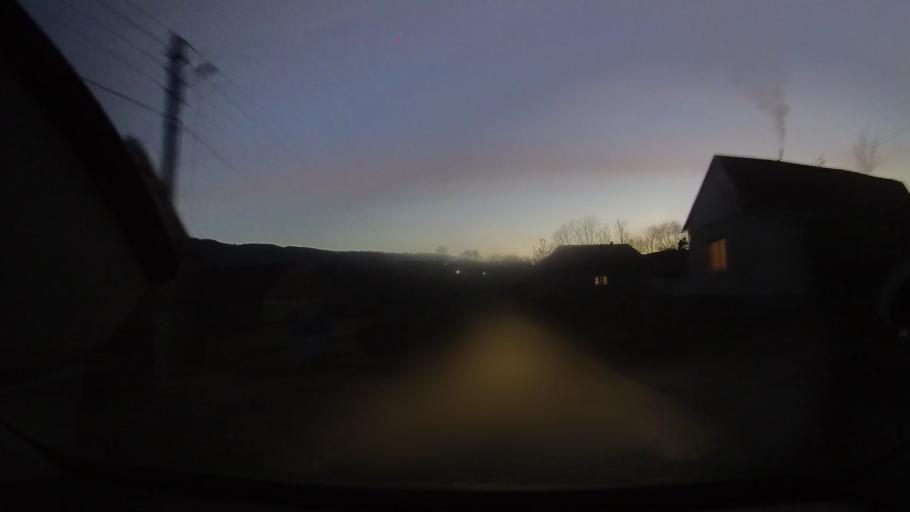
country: RO
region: Bihor
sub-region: Comuna Varciorog
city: Varciorog
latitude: 46.9812
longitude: 22.3273
